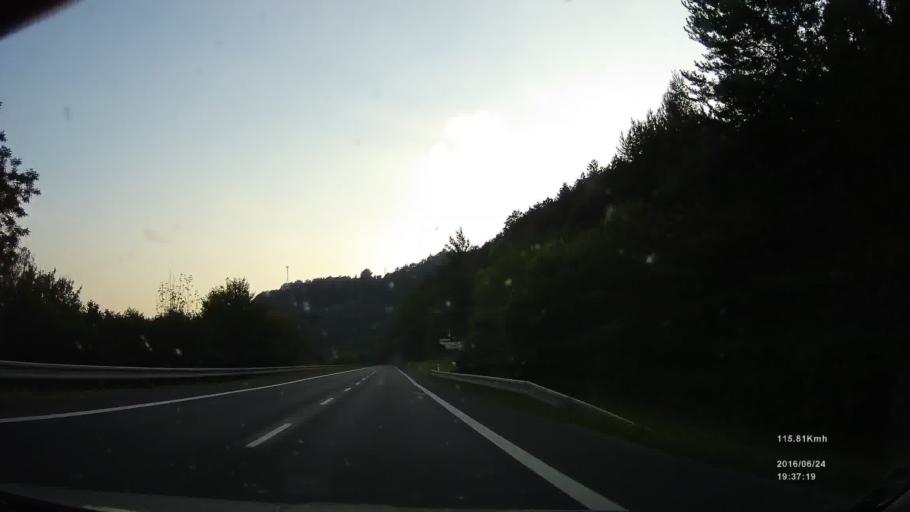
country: SK
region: Banskobystricky
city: Hrochot,Slovakia
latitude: 48.8161
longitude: 19.4197
